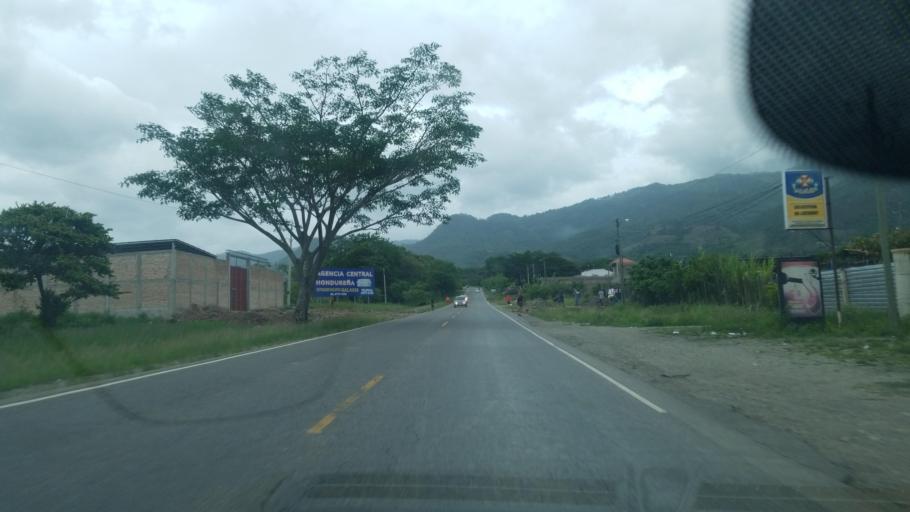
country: HN
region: Ocotepeque
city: Santa Lucia
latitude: 14.4183
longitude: -89.1928
